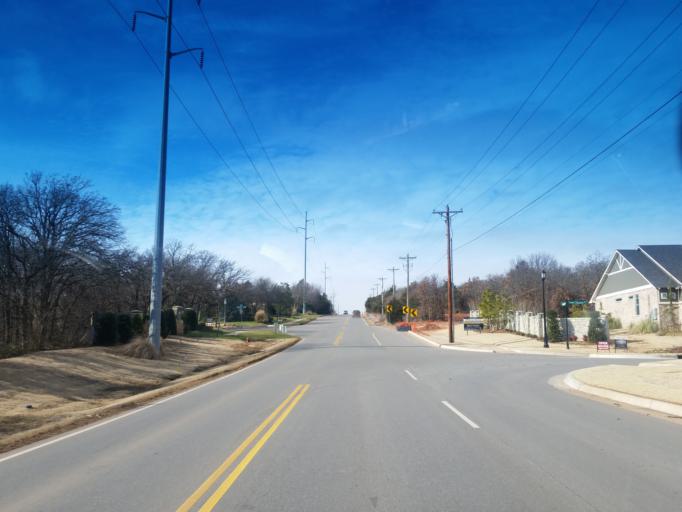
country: US
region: Oklahoma
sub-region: Oklahoma County
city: Edmond
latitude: 35.6672
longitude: -97.4356
